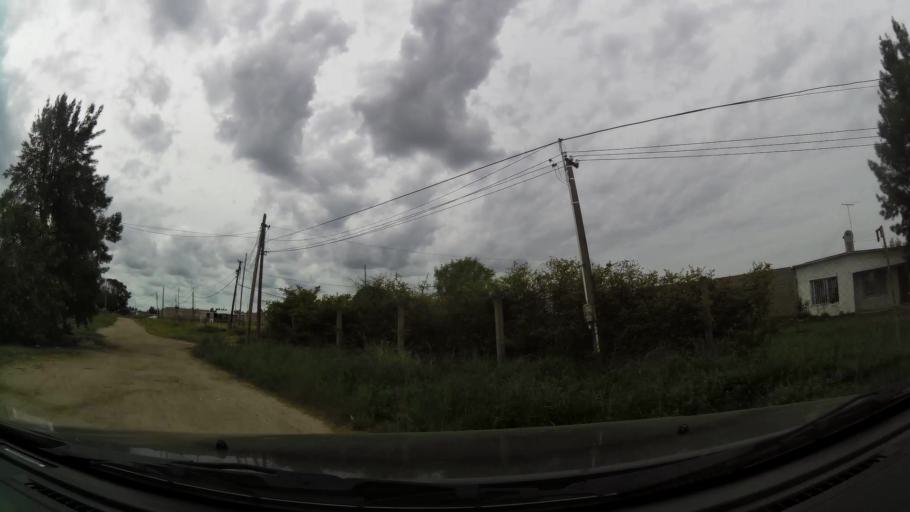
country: UY
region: Canelones
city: Las Piedras
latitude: -34.7120
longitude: -56.2035
